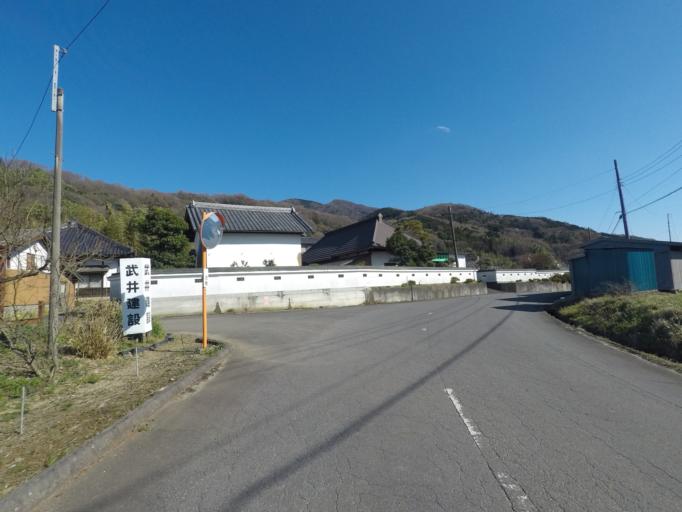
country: JP
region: Ibaraki
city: Makabe
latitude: 36.2441
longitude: 140.0714
